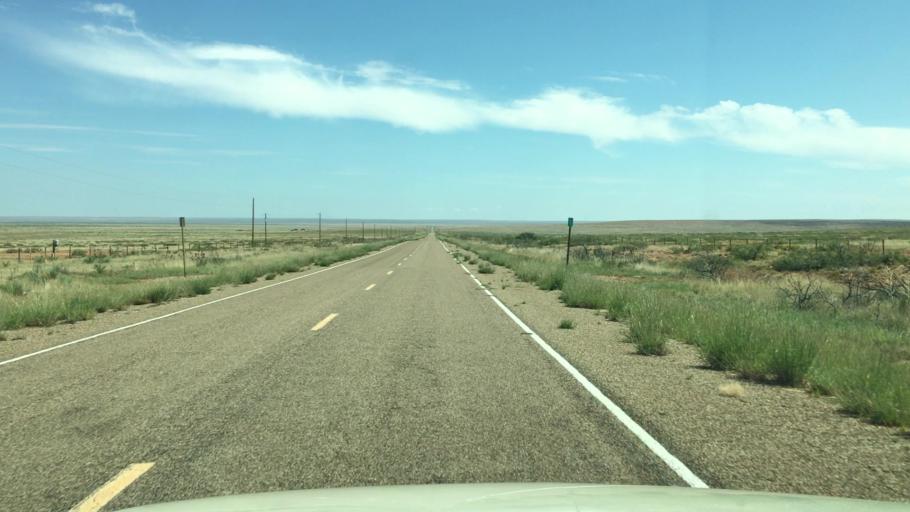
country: US
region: New Mexico
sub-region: De Baca County
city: Fort Sumner
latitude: 33.9860
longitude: -104.5725
